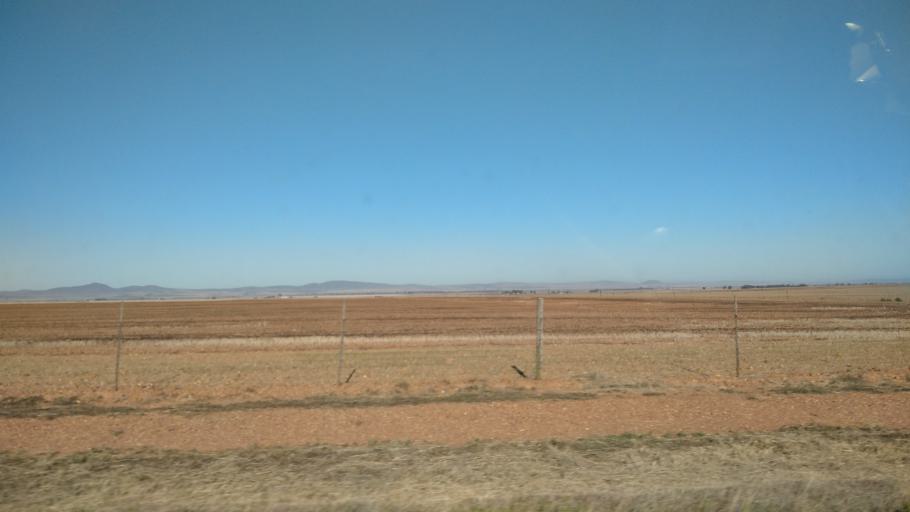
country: ZA
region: Western Cape
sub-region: West Coast District Municipality
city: Moorreesburg
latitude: -33.3155
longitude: 18.6227
